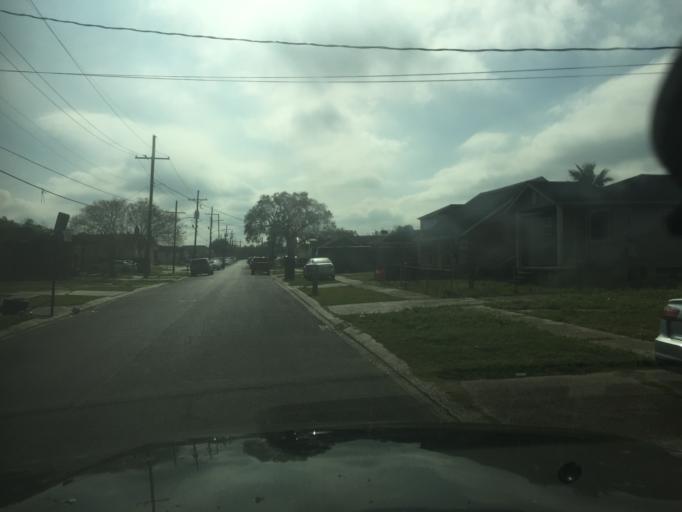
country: US
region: Louisiana
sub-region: Orleans Parish
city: New Orleans
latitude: 29.9970
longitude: -90.0408
